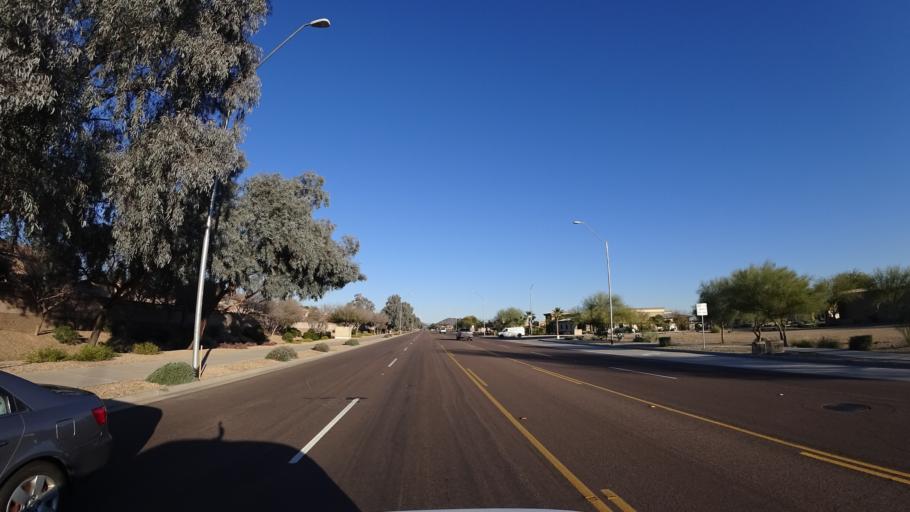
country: US
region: Arizona
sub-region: Maricopa County
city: Sun City
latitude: 33.6817
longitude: -112.2276
